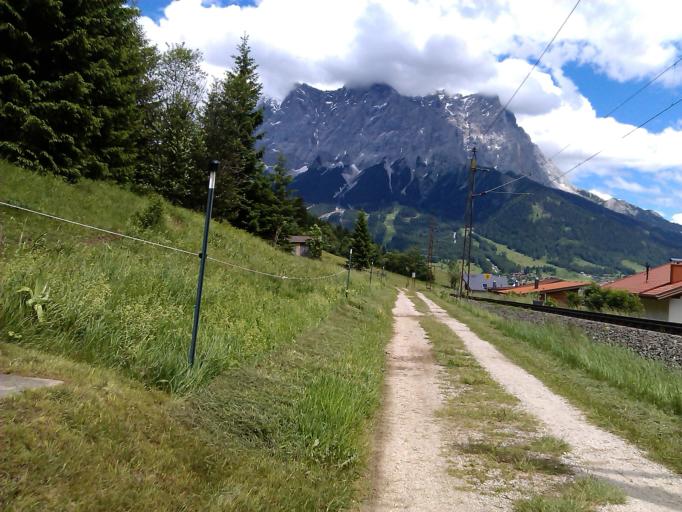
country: AT
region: Tyrol
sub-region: Politischer Bezirk Reutte
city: Lermoos
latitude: 47.4049
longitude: 10.8857
